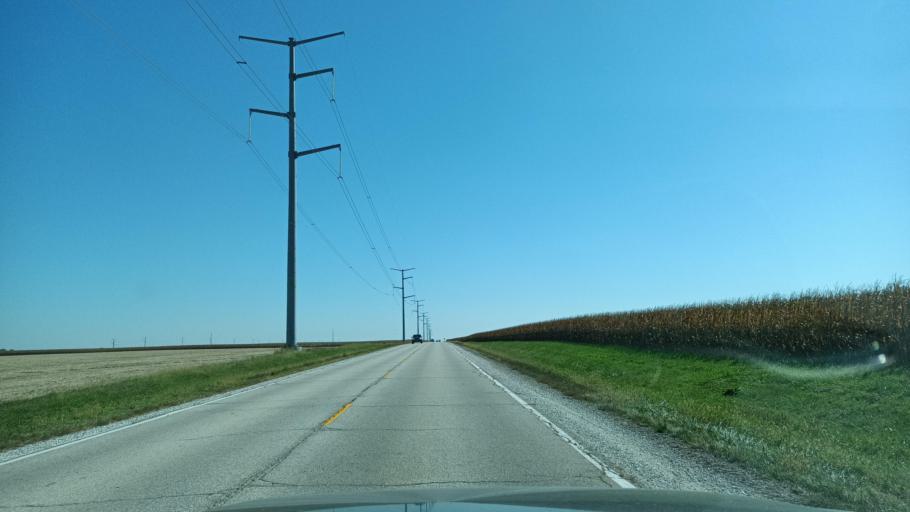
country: US
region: Illinois
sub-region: Peoria County
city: Elmwood
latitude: 40.9023
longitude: -89.9950
